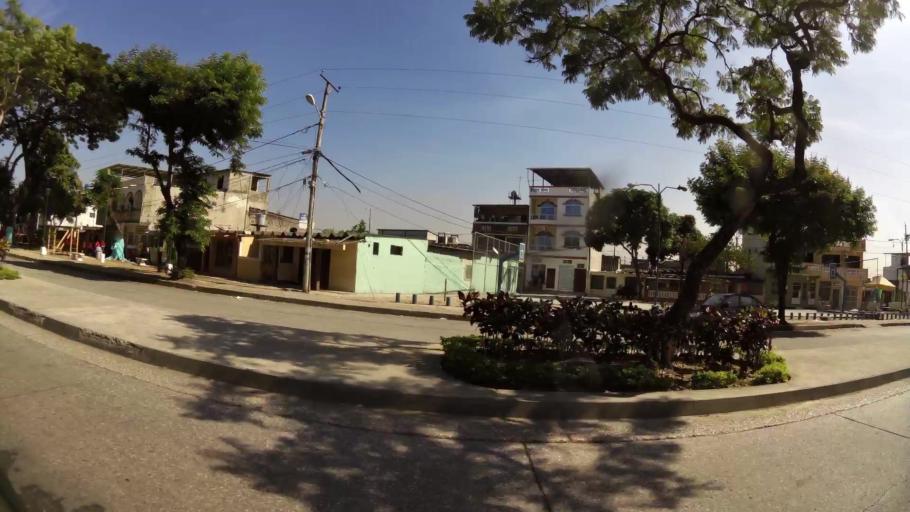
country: EC
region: Guayas
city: Eloy Alfaro
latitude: -2.1263
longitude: -79.8922
